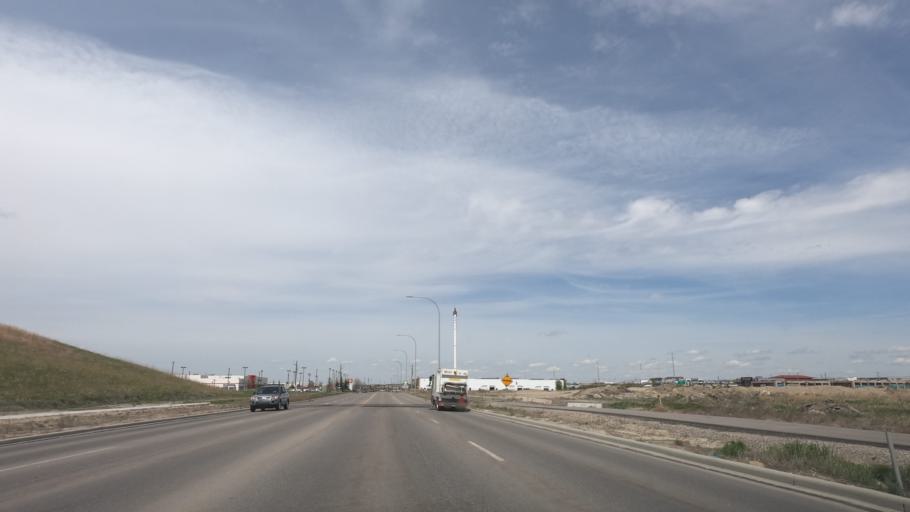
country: CA
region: Alberta
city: Airdrie
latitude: 51.2558
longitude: -114.0051
